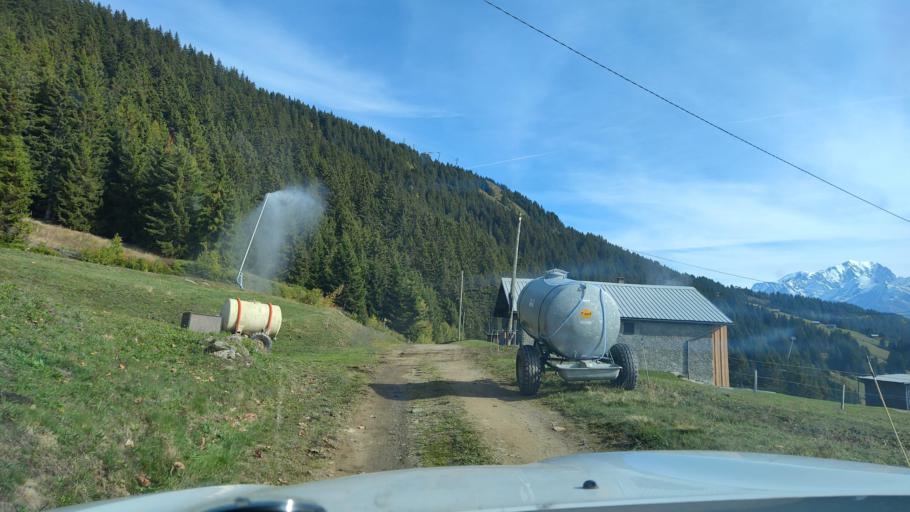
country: FR
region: Rhone-Alpes
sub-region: Departement de la Savoie
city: Beaufort
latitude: 45.7385
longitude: 6.4969
